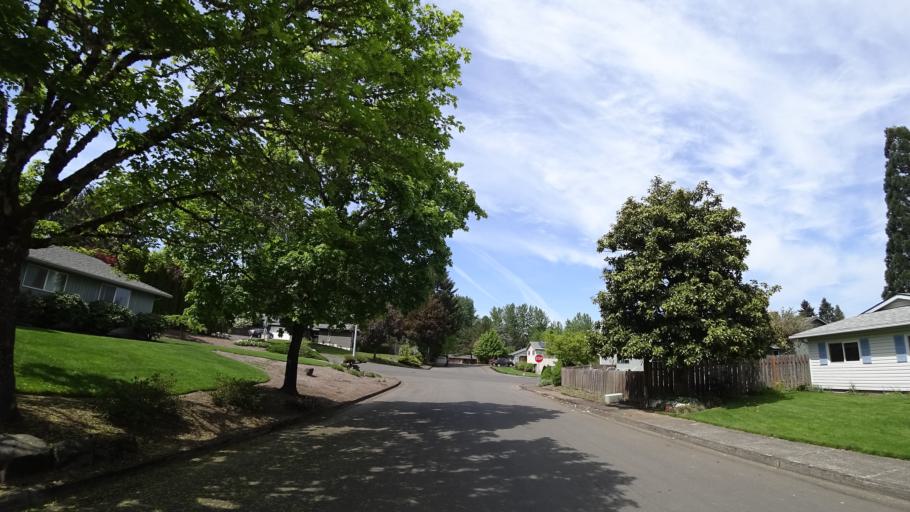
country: US
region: Oregon
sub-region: Washington County
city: Aloha
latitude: 45.4808
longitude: -122.8923
